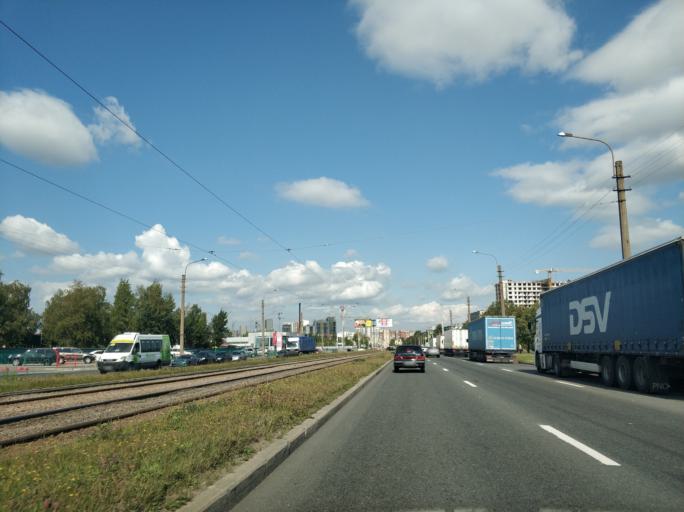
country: RU
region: St.-Petersburg
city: Obukhovo
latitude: 59.8919
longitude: 30.4630
